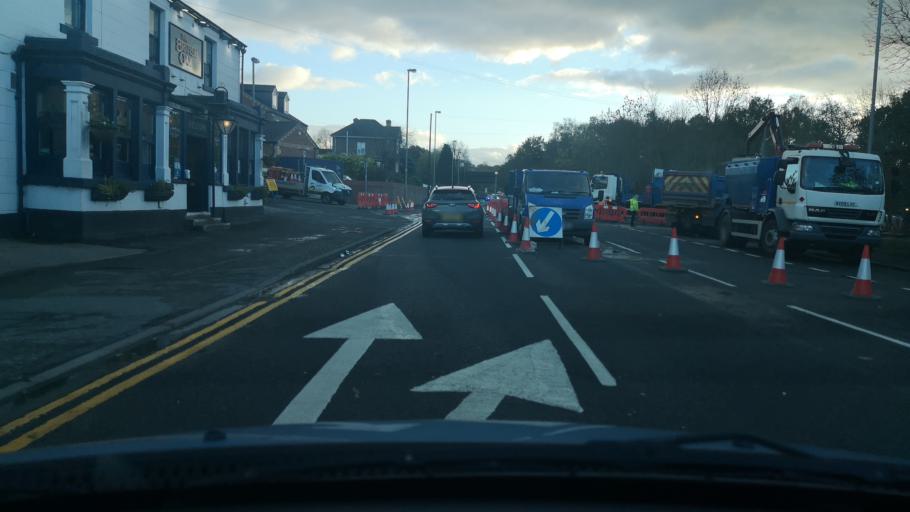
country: GB
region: England
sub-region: City and Borough of Wakefield
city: Crigglestone
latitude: 53.6425
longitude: -1.5467
